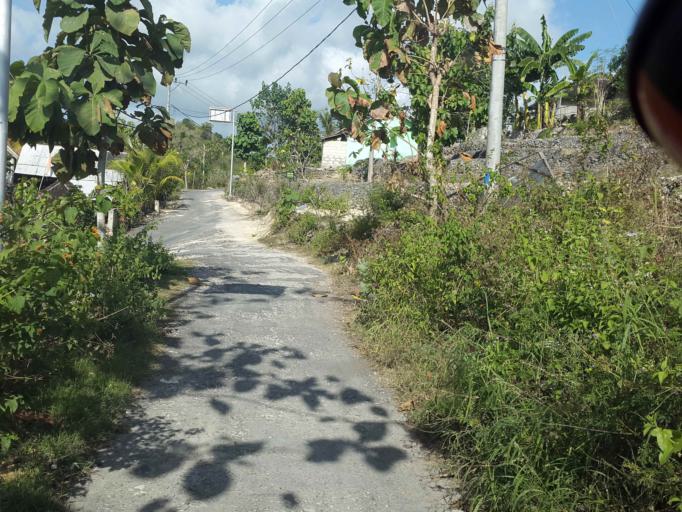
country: ID
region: Bali
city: Pondokkaha Kelod
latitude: -8.7414
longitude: 115.4909
